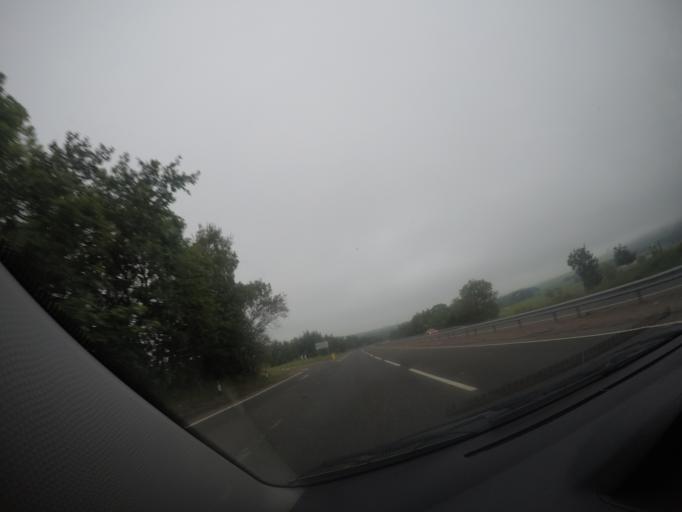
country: GB
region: Scotland
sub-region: Angus
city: Forfar
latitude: 56.5842
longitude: -2.9133
